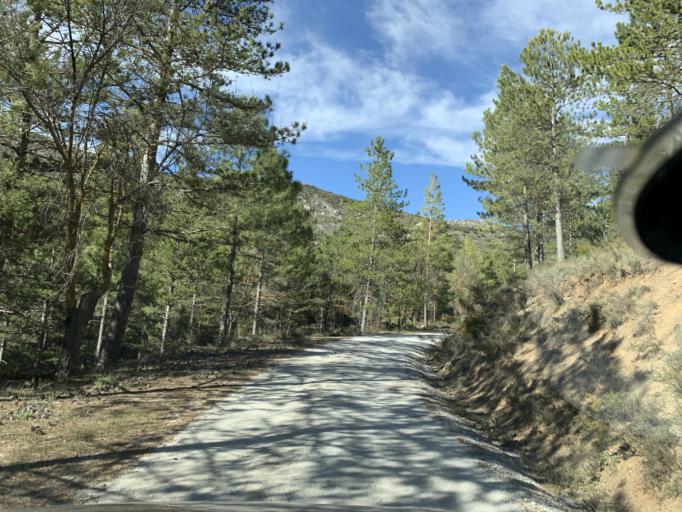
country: ES
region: Andalusia
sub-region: Provincia de Granada
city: Beas de Granada
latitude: 37.2387
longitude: -3.4469
